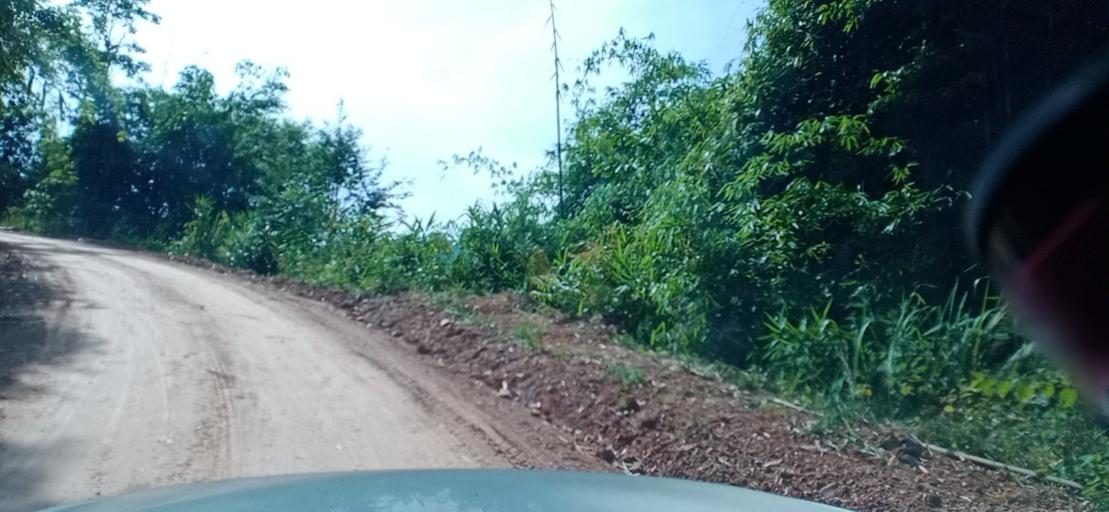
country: TH
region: Changwat Bueng Kan
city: Pak Khat
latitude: 18.6386
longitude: 103.2451
